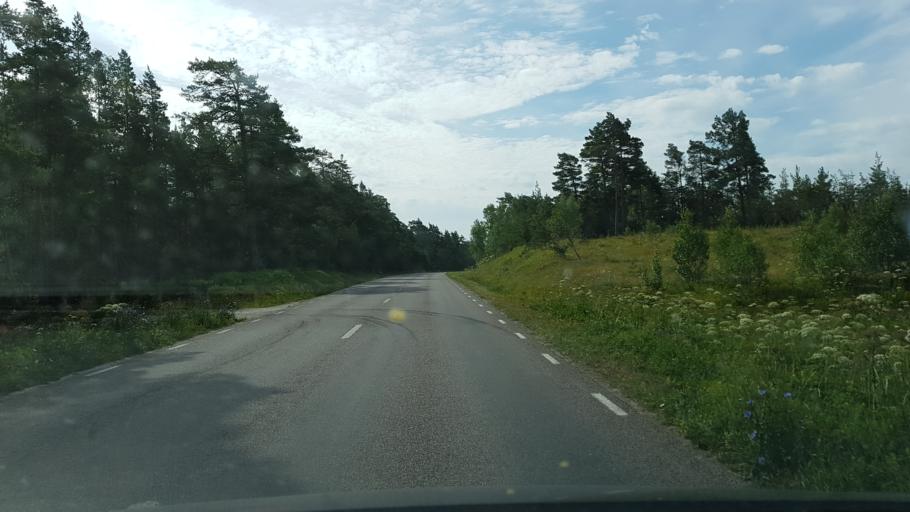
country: SE
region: Gotland
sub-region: Gotland
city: Hemse
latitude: 57.4577
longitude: 18.5760
